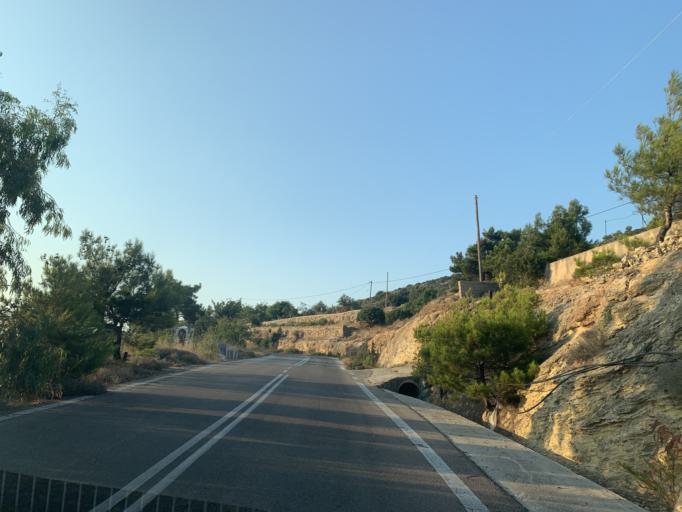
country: GR
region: North Aegean
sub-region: Chios
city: Thymiana
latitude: 38.2901
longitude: 25.9307
